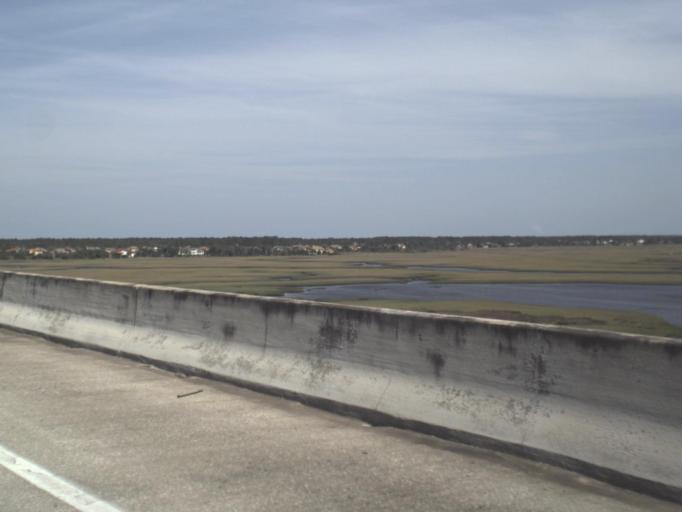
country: US
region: Florida
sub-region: Saint Johns County
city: Ponte Vedra Beach
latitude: 30.2572
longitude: -81.4295
